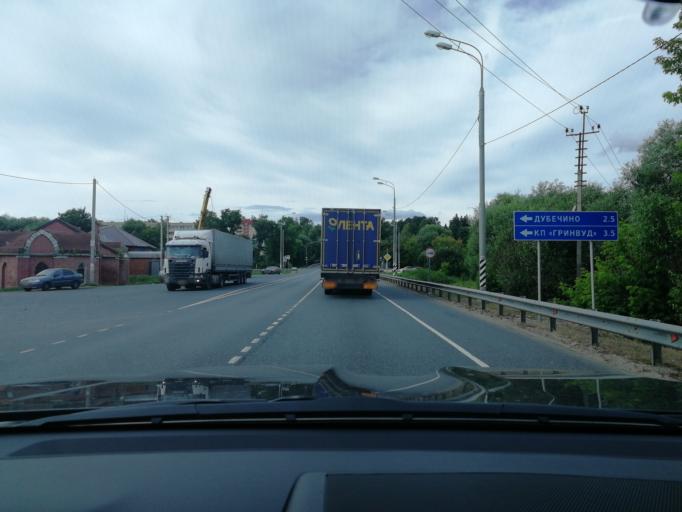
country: RU
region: Moskovskaya
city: Popovo
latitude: 55.0555
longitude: 37.7638
